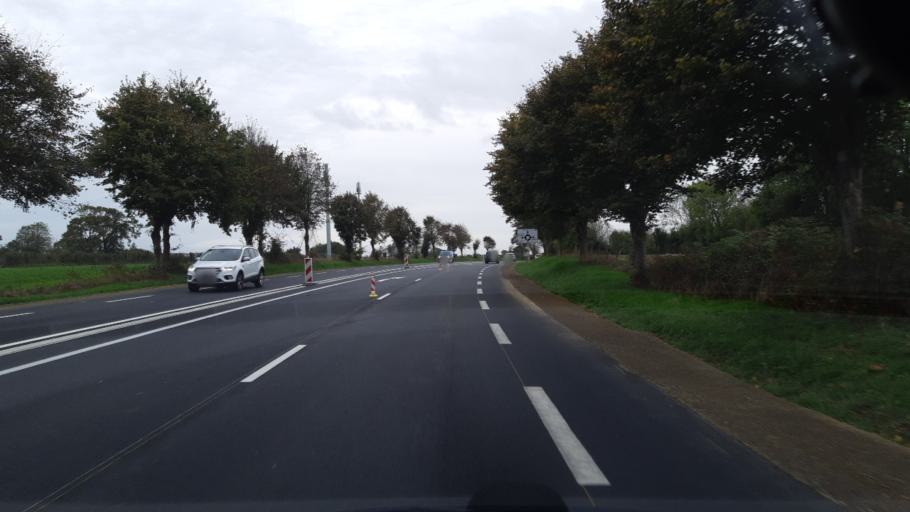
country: FR
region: Lower Normandy
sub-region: Departement de la Manche
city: Brehal
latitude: 48.8983
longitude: -1.5006
